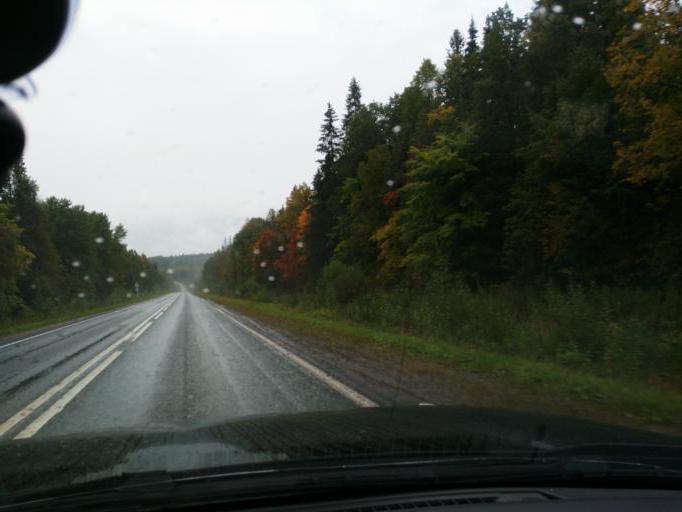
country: RU
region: Perm
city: Yugo-Kamskiy
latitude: 57.5855
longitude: 55.6737
